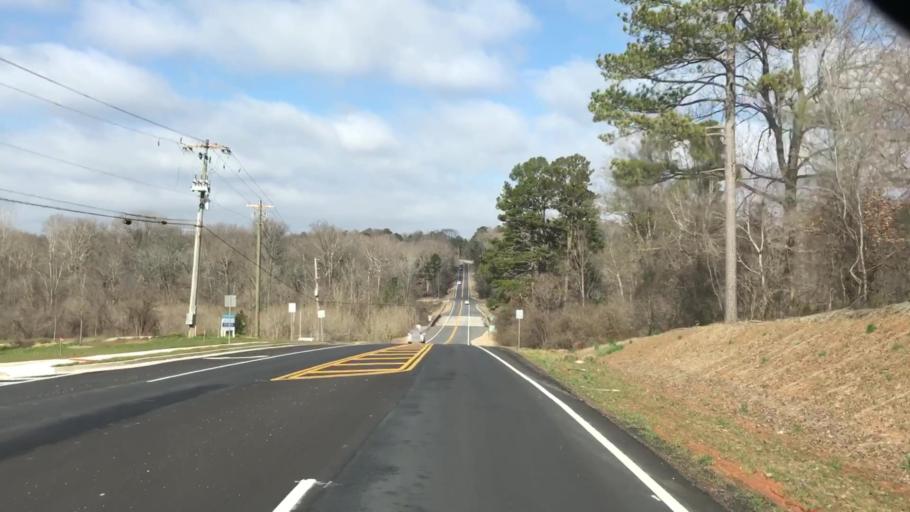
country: US
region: Georgia
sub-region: Jackson County
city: Braselton
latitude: 34.1273
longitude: -83.8302
